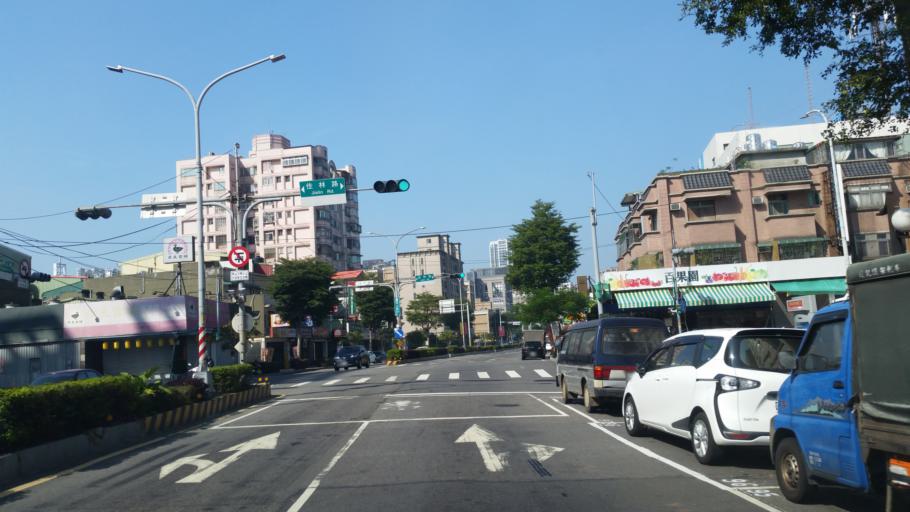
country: TW
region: Taipei
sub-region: Taipei
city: Banqiao
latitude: 25.0795
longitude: 121.3858
